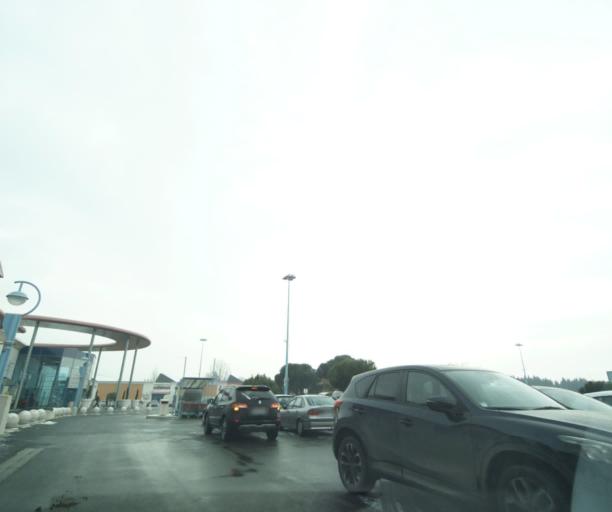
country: FR
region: Auvergne
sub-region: Departement du Puy-de-Dome
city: Menetrol
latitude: 45.8756
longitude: 3.1185
